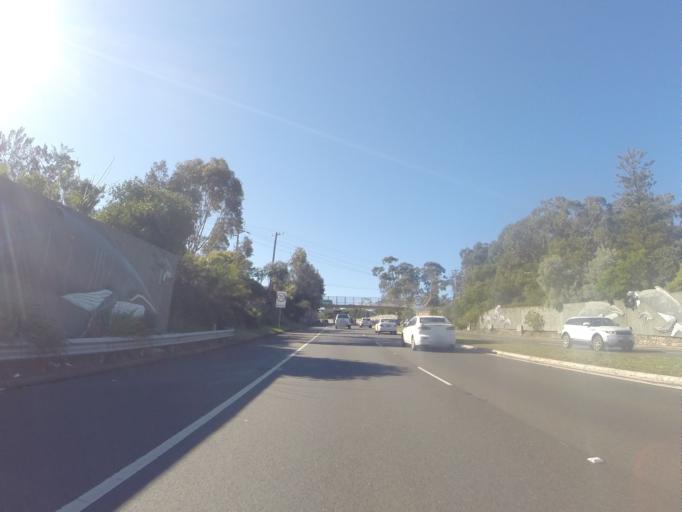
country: AU
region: New South Wales
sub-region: Sutherland Shire
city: Kirrawee
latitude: -34.0390
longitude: 151.0628
